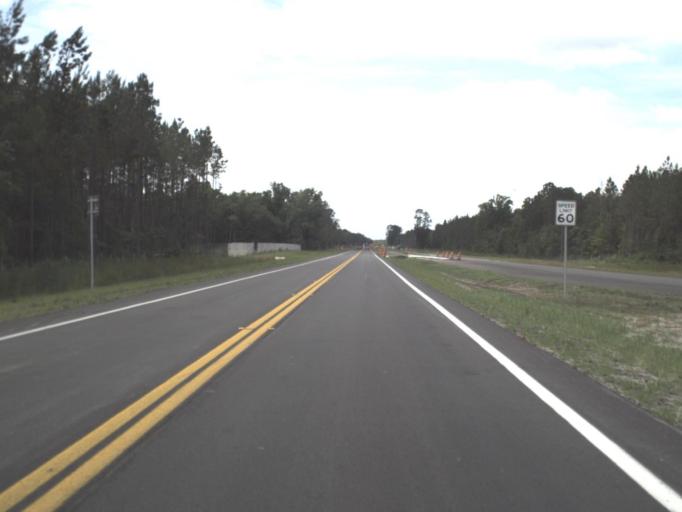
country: US
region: Florida
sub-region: Nassau County
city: Nassau Village-Ratliff
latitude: 30.4412
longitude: -81.9192
